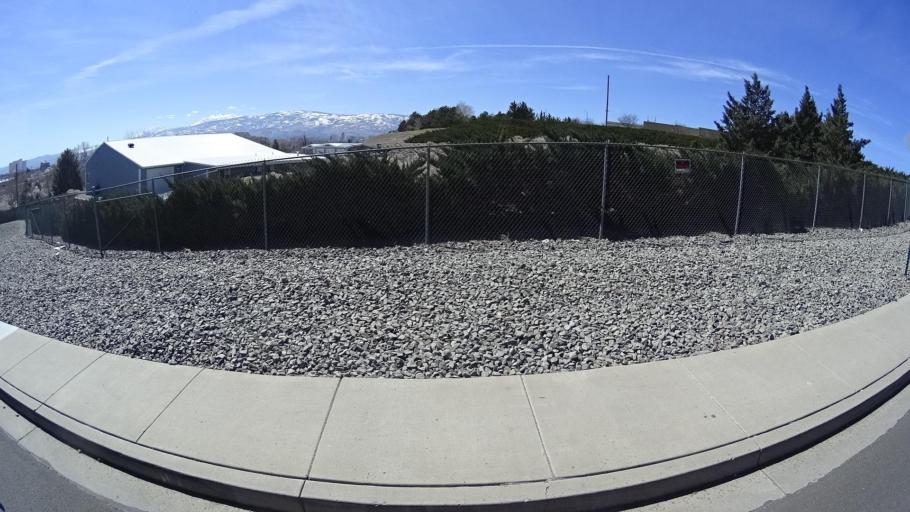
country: US
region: Nevada
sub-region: Washoe County
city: Sparks
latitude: 39.5536
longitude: -119.7809
